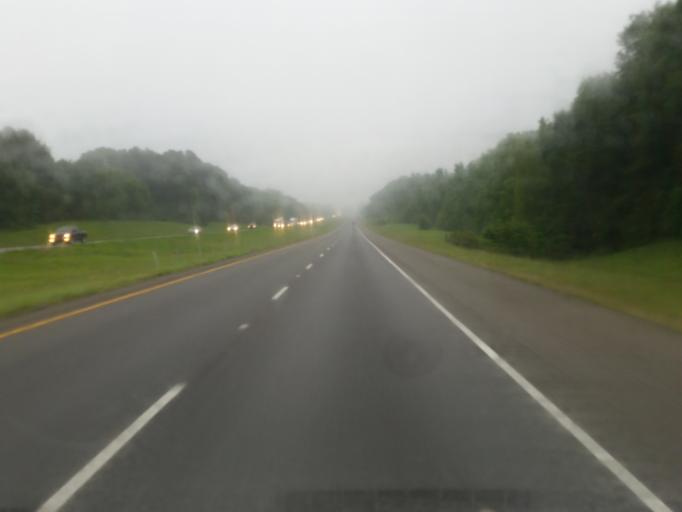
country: US
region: Louisiana
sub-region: Bossier Parish
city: Red Chute
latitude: 32.5419
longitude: -93.5943
